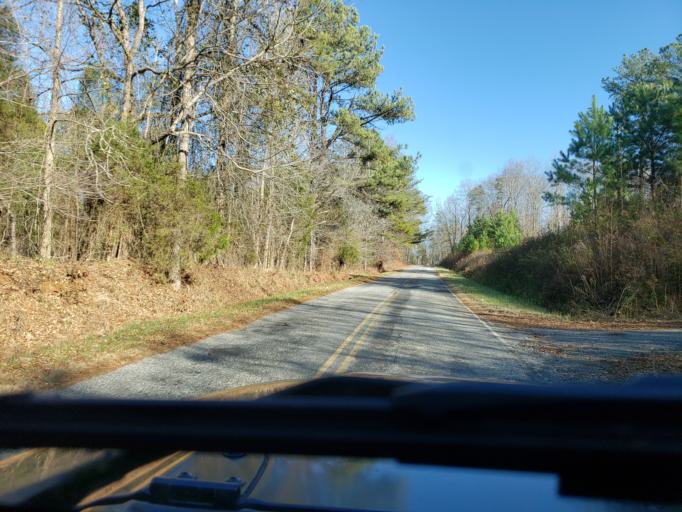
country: US
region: North Carolina
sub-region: Cleveland County
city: White Plains
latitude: 35.1666
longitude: -81.4130
